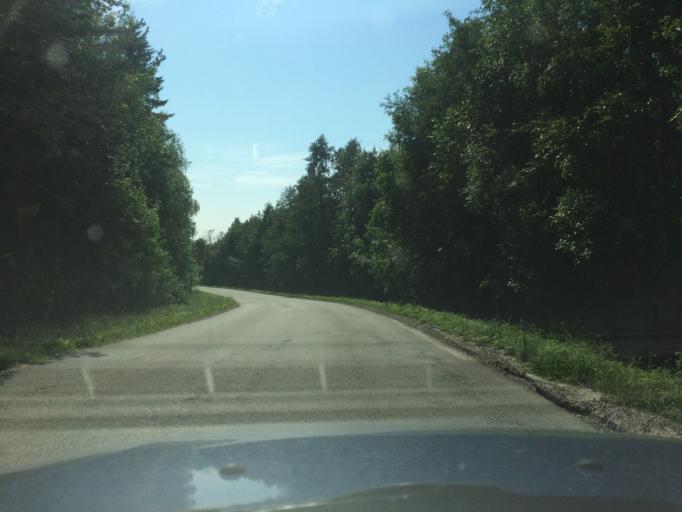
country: SE
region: Norrbotten
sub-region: Pitea Kommun
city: Norrfjarden
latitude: 65.3748
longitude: 21.3909
